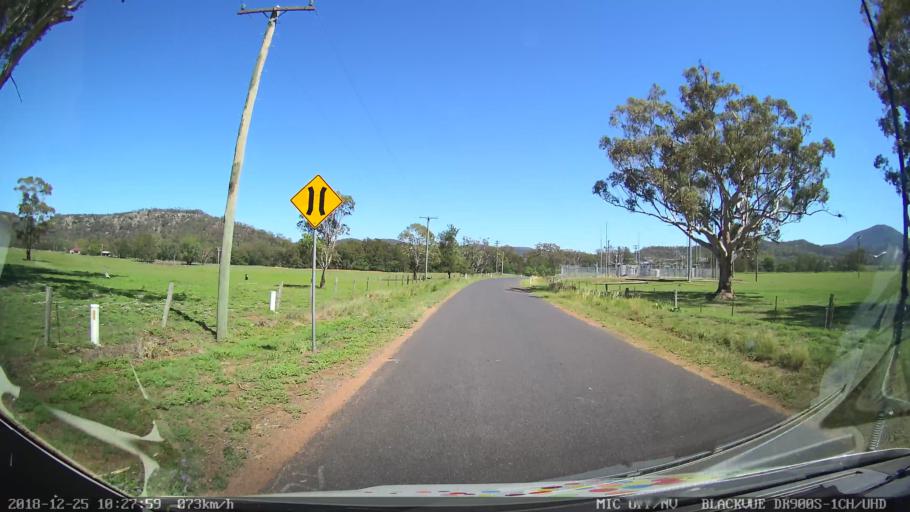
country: AU
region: New South Wales
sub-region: Muswellbrook
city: Denman
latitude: -32.3859
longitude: 150.4668
